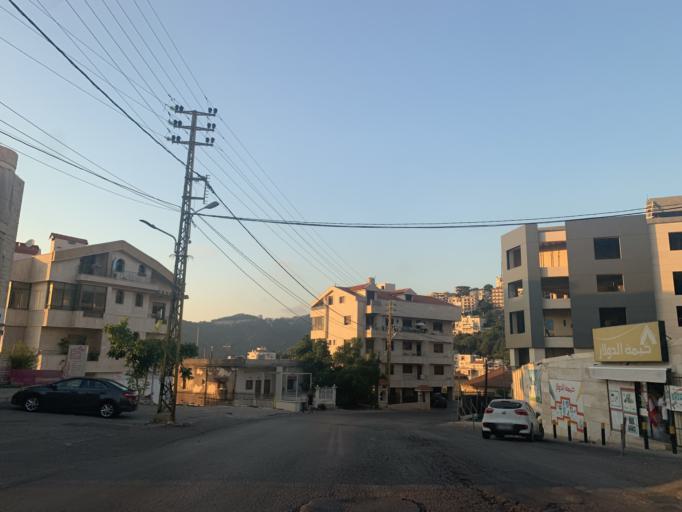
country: LB
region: Mont-Liban
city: Djounie
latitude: 33.9554
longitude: 35.6428
